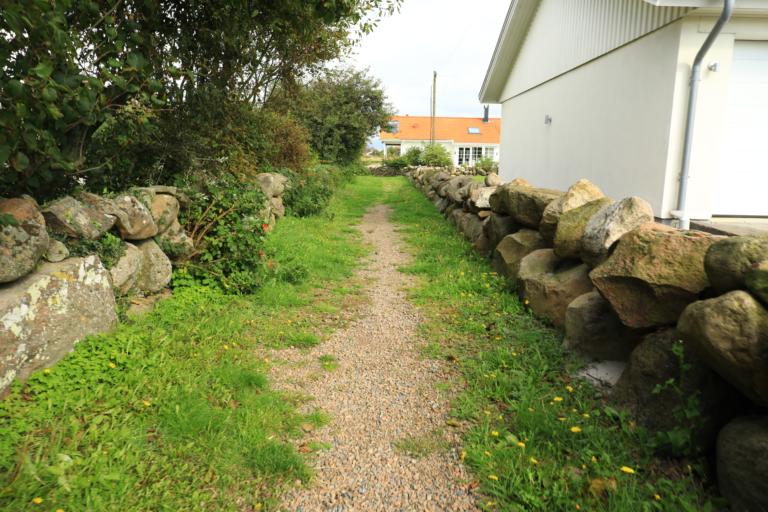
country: SE
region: Halland
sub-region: Varbergs Kommun
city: Traslovslage
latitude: 57.0707
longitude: 12.2577
